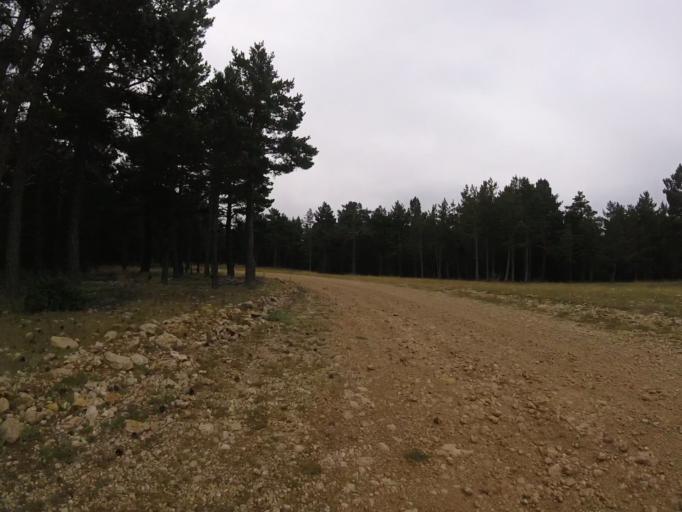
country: ES
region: Aragon
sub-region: Provincia de Teruel
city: Valdelinares
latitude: 40.3713
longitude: -0.6227
